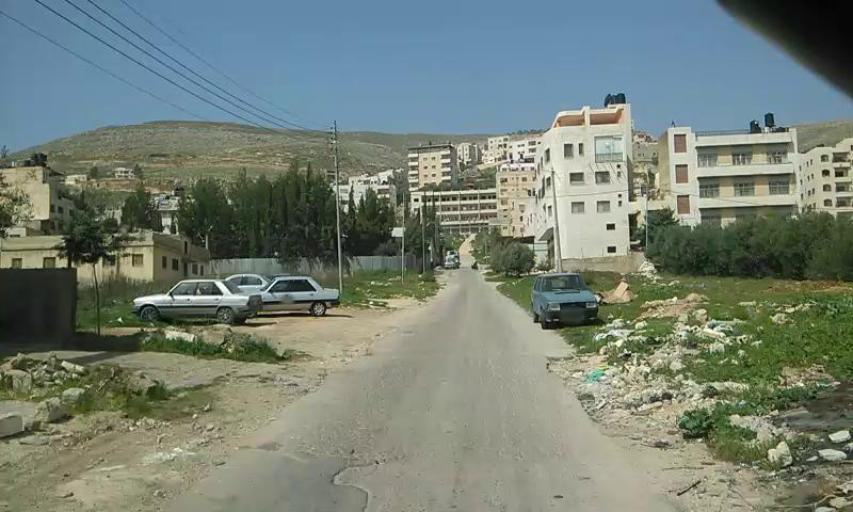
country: PS
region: West Bank
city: `Azmut
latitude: 32.2222
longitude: 35.2979
